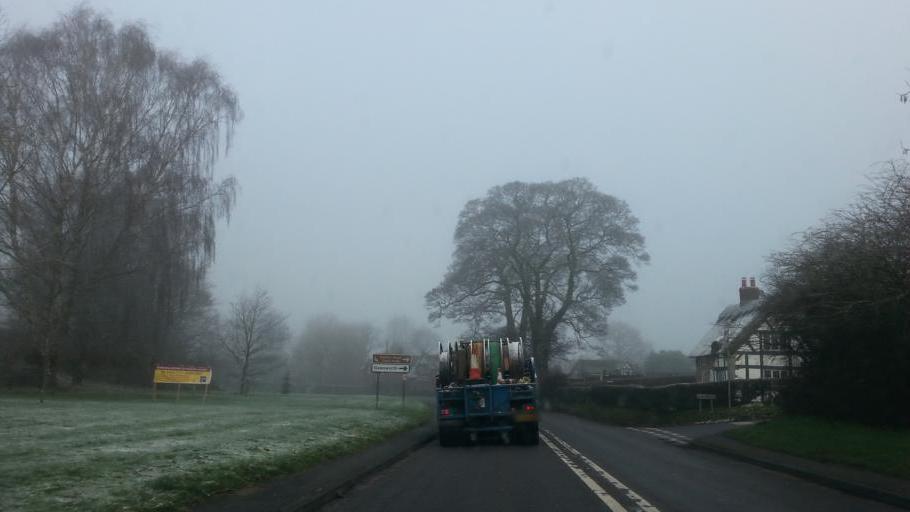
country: GB
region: England
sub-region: Cheshire East
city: Siddington
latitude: 53.2105
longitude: -2.2258
